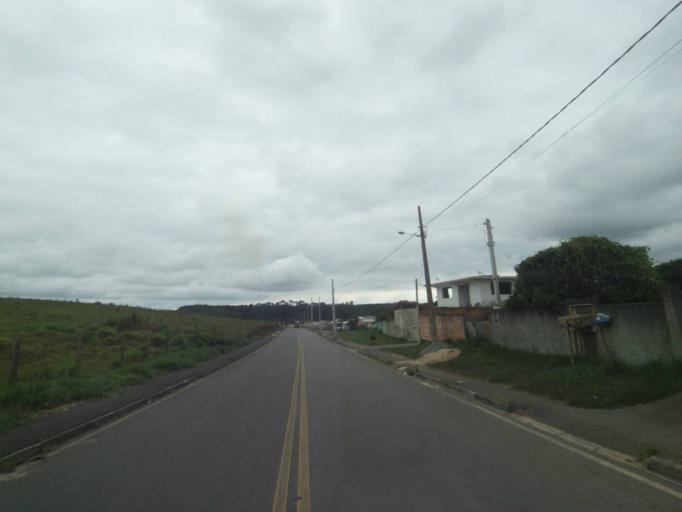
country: BR
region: Parana
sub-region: Quatro Barras
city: Quatro Barras
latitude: -25.3497
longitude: -49.1160
